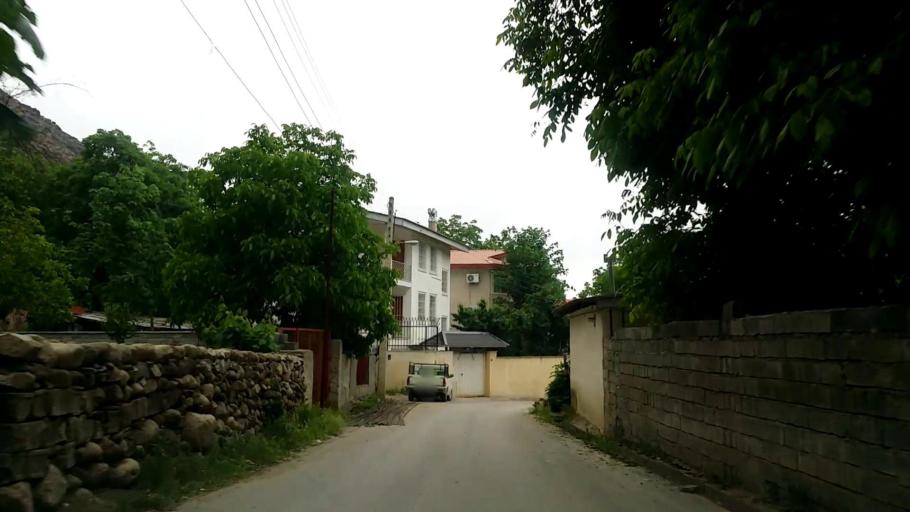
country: IR
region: Mazandaran
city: `Abbasabad
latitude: 36.4982
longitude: 51.1412
